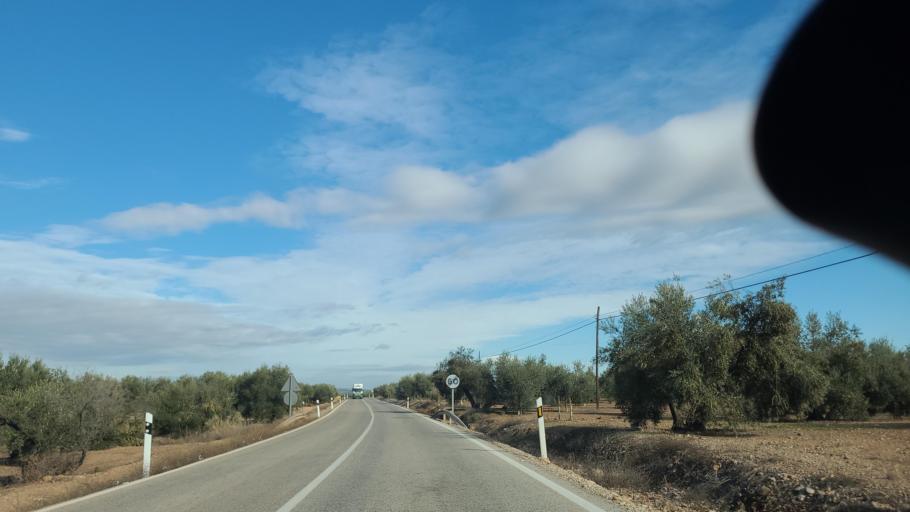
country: ES
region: Andalusia
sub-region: Provincia de Jaen
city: Espeluy
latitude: 38.0231
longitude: -3.8767
